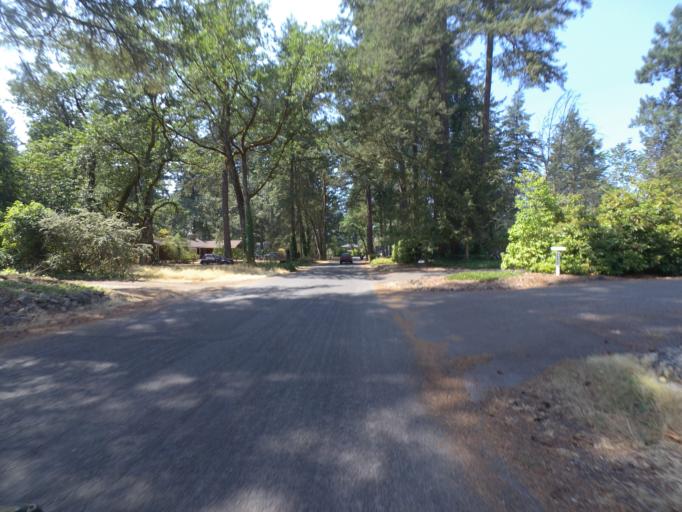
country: US
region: Washington
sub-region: Pierce County
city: Lakewood
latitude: 47.1581
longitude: -122.5235
